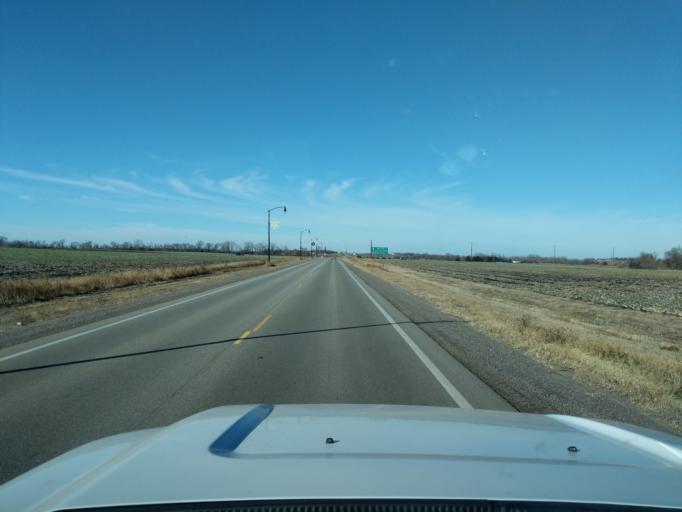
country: US
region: Minnesota
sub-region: Yellow Medicine County
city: Granite Falls
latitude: 44.7686
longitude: -95.5394
